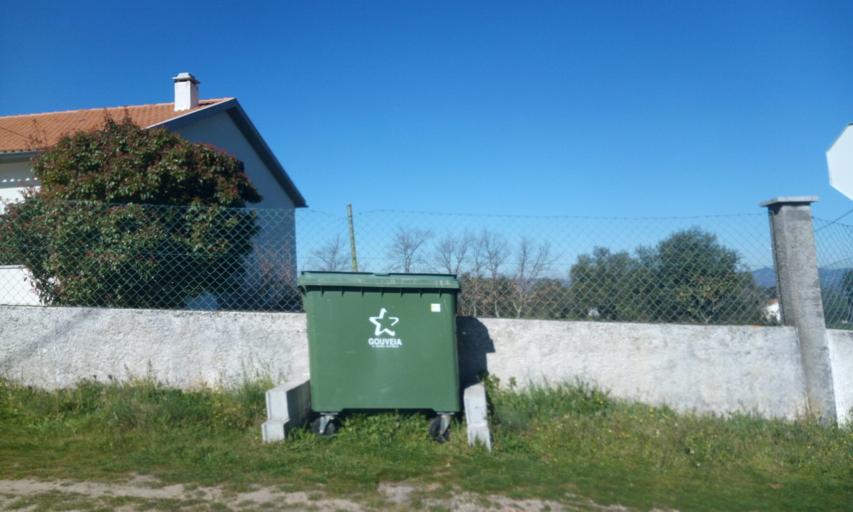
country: PT
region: Guarda
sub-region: Fornos de Algodres
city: Fornos de Algodres
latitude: 40.5260
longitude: -7.5576
